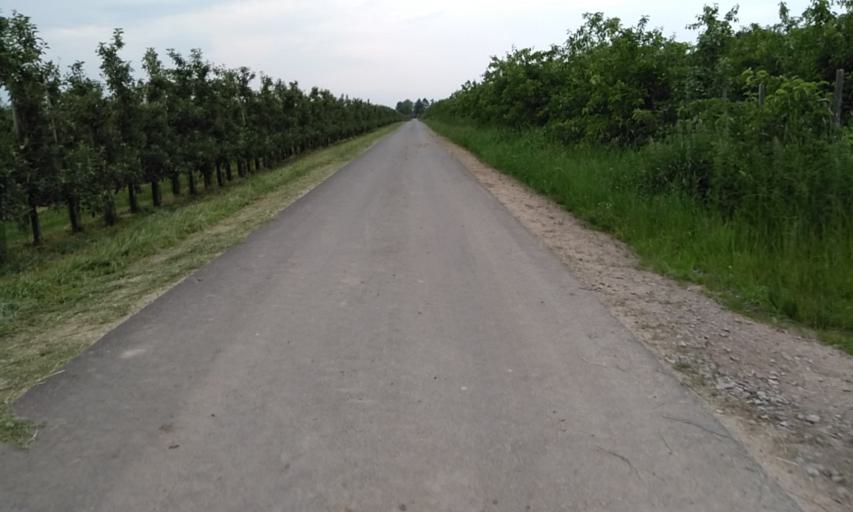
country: DE
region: Lower Saxony
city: Jork
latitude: 53.5085
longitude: 9.6878
